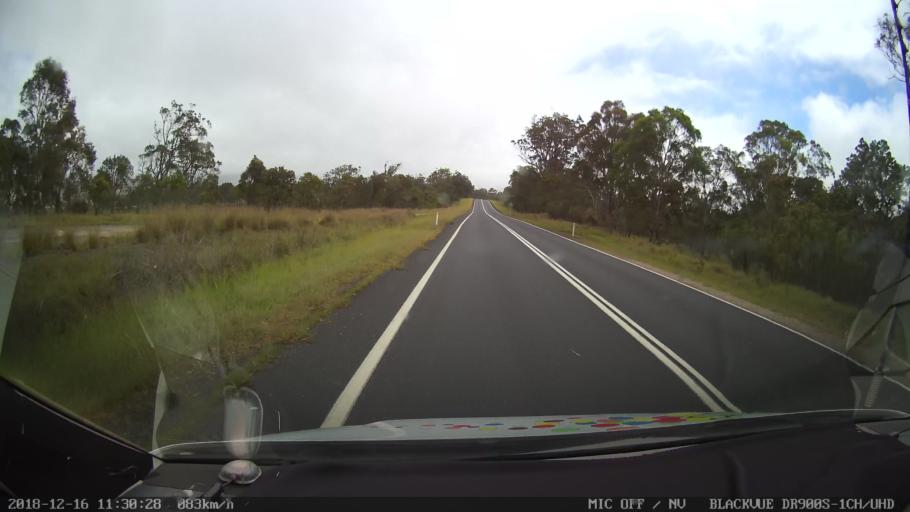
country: AU
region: New South Wales
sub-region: Tenterfield Municipality
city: Carrolls Creek
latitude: -29.0323
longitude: 152.1207
